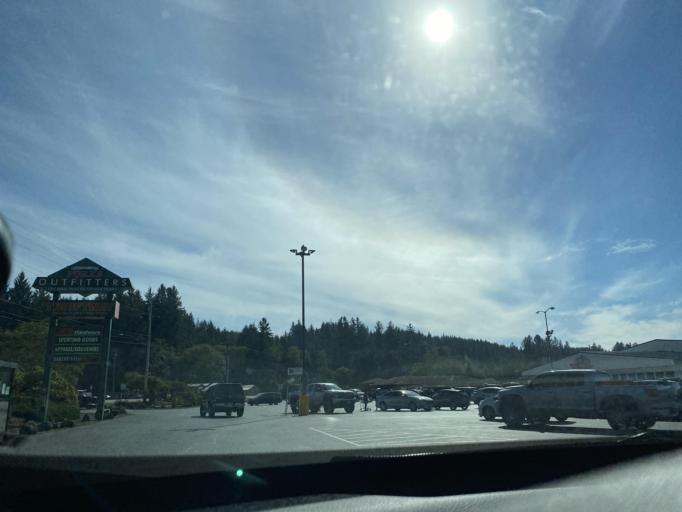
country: US
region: Washington
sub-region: Clallam County
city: Forks
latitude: 47.9419
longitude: -124.3859
